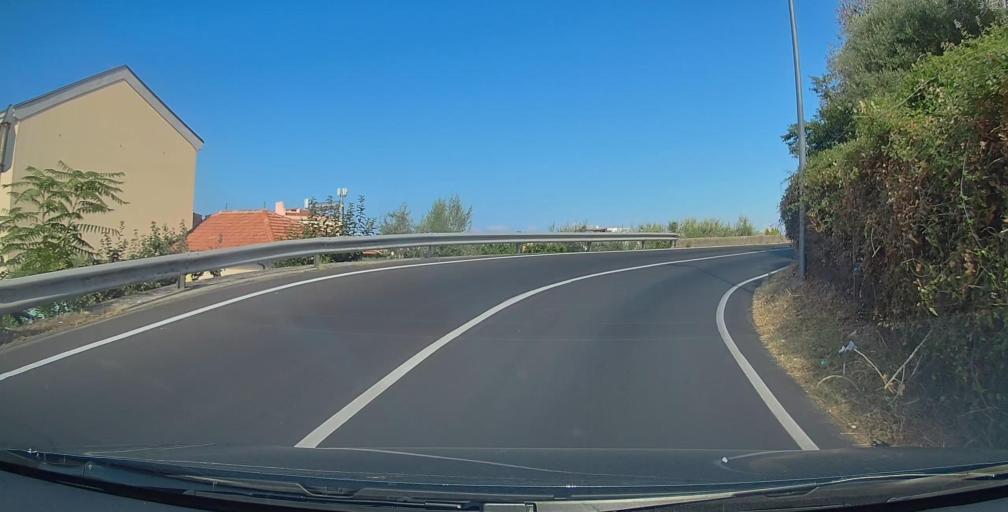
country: IT
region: Sicily
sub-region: Messina
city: Patti
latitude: 38.1512
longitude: 14.9686
